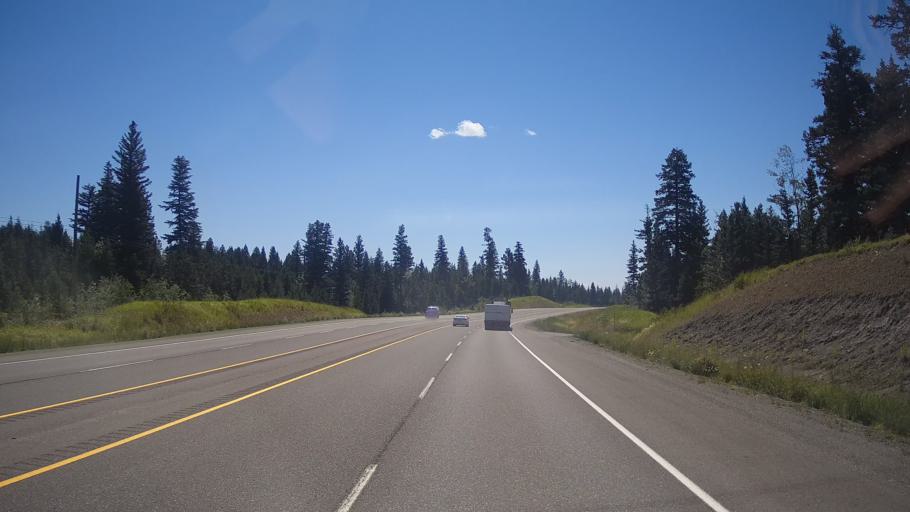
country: CA
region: British Columbia
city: Cache Creek
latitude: 51.4106
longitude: -121.3761
